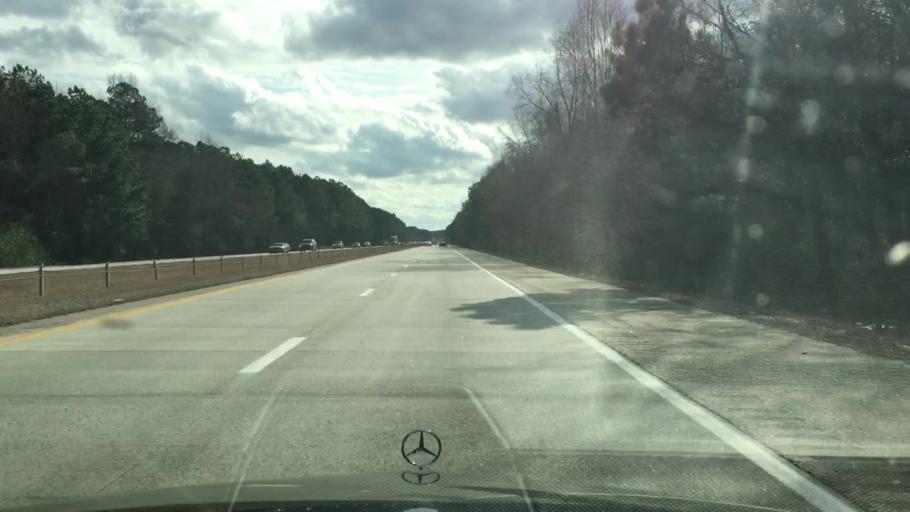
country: US
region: North Carolina
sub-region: Johnston County
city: Benson
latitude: 35.5001
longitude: -78.5542
